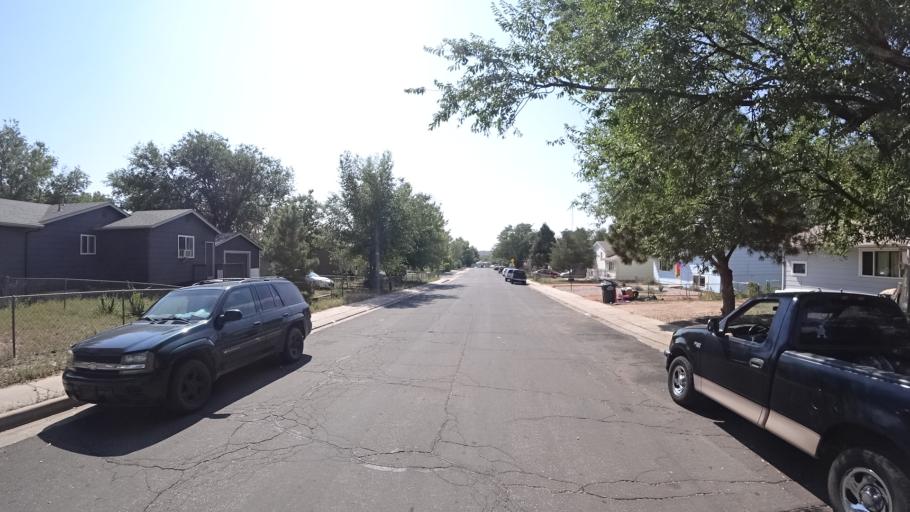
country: US
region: Colorado
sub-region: El Paso County
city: Colorado Springs
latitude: 38.8212
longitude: -104.7862
